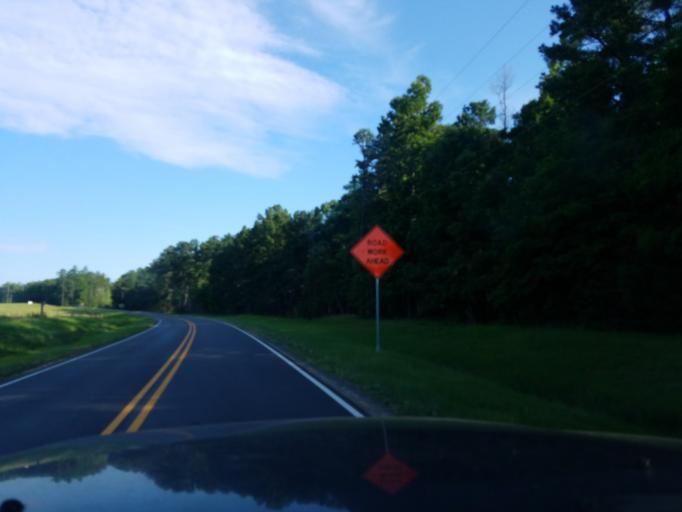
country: US
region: North Carolina
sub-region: Granville County
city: Butner
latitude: 36.1745
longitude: -78.7943
